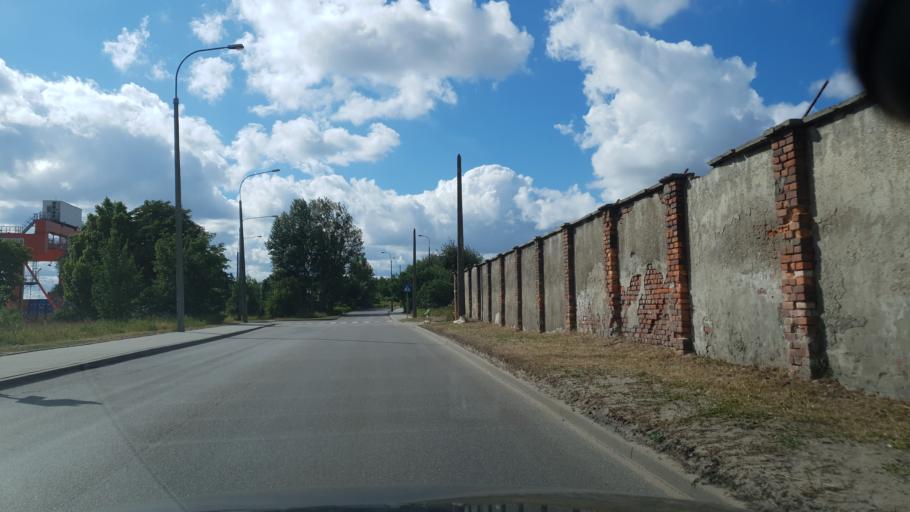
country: PL
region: Pomeranian Voivodeship
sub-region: Gdynia
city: Gdynia
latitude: 54.5457
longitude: 18.5224
